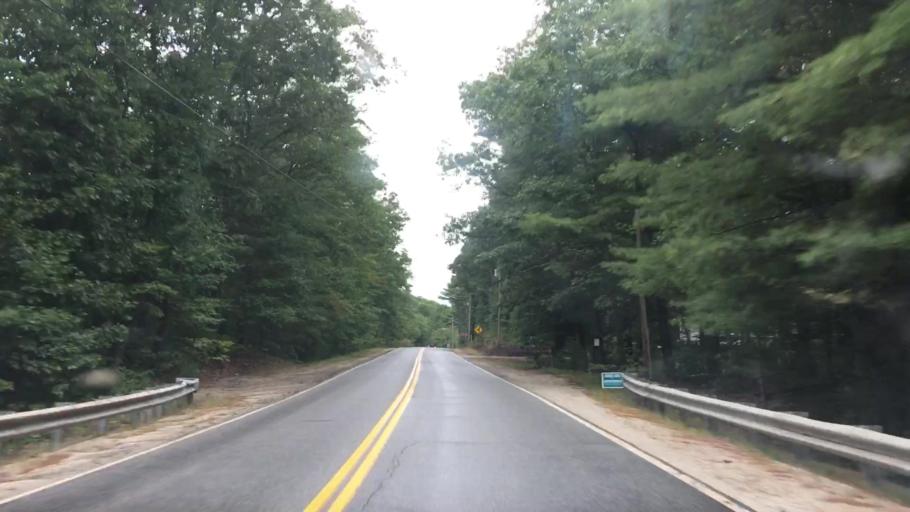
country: US
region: Maine
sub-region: Cumberland County
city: Raymond
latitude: 43.9500
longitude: -70.4630
